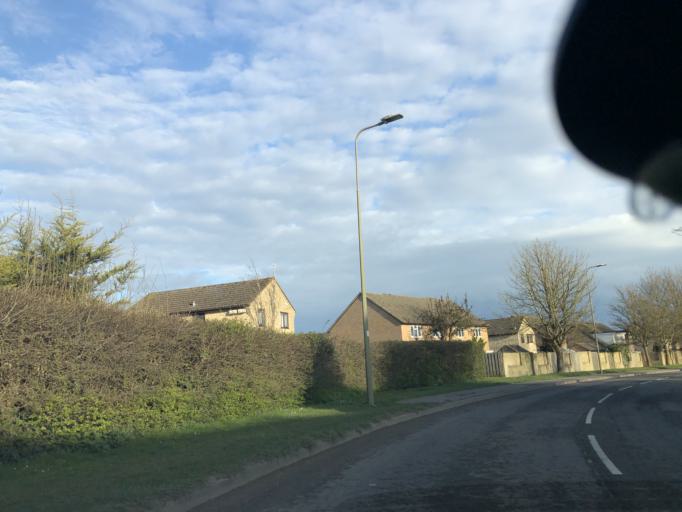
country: GB
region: England
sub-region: Oxfordshire
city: Witney
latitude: 51.7784
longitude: -1.5078
